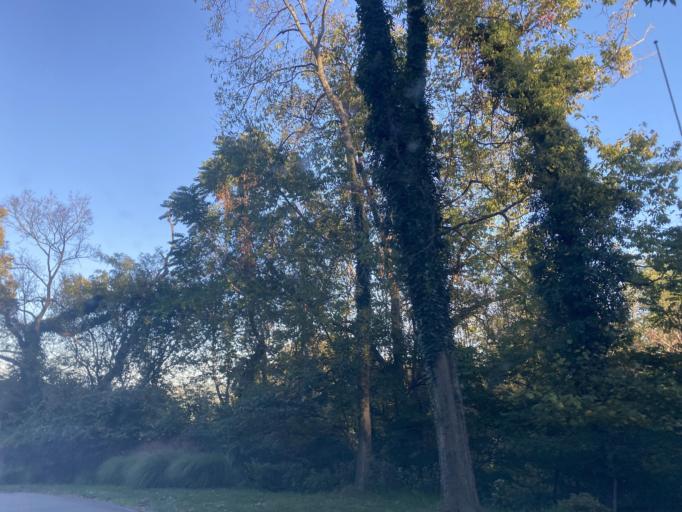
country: US
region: Kentucky
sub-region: Campbell County
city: Fort Thomas
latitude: 39.1022
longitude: -84.4472
